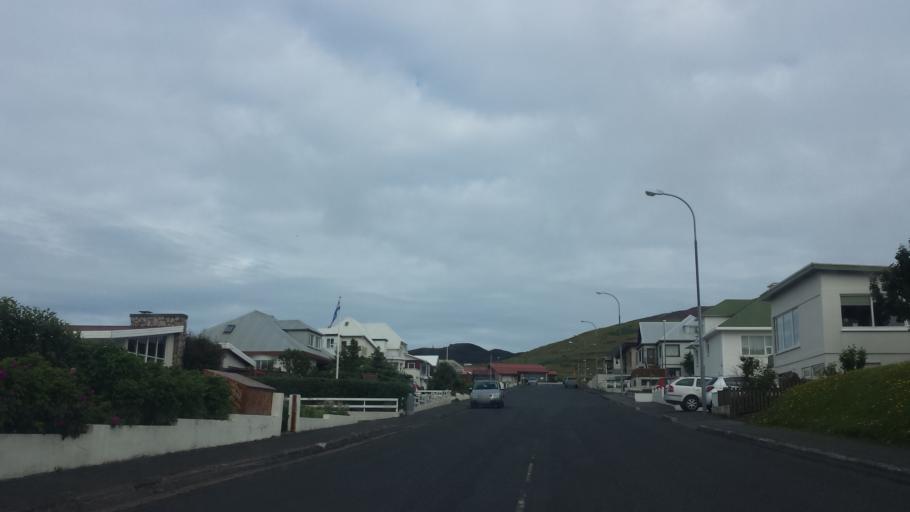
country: IS
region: South
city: Vestmannaeyjar
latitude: 63.4379
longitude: -20.2668
